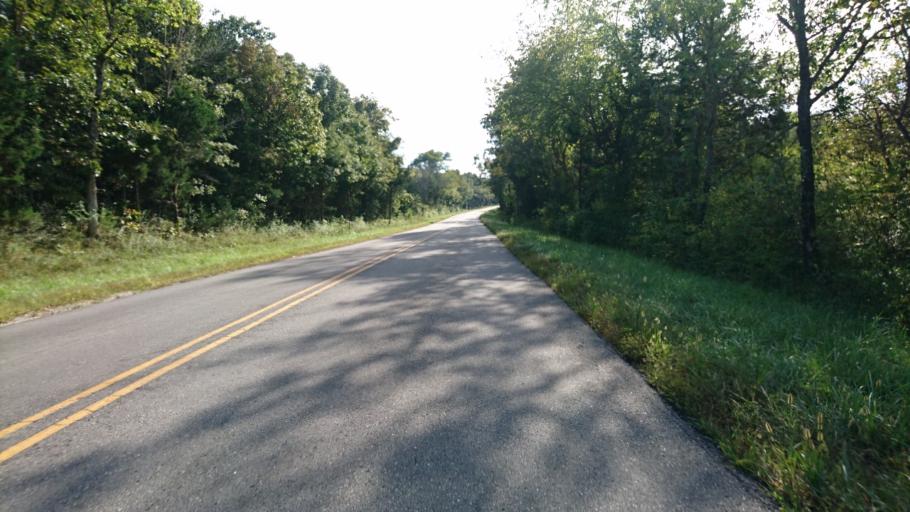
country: US
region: Missouri
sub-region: Crawford County
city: Cuba
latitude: 38.1014
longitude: -91.3498
